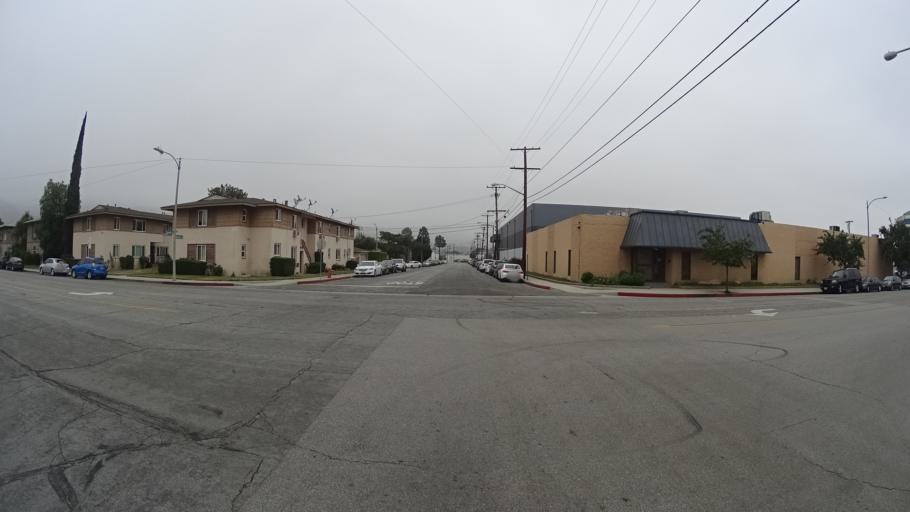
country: US
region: California
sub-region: Los Angeles County
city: Burbank
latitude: 34.1937
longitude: -118.3360
